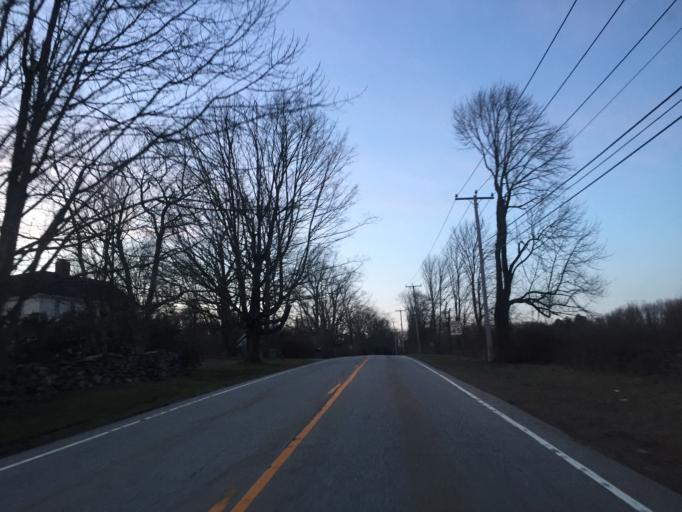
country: US
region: Connecticut
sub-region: Windham County
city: East Brooklyn
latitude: 41.8131
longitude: -71.9562
